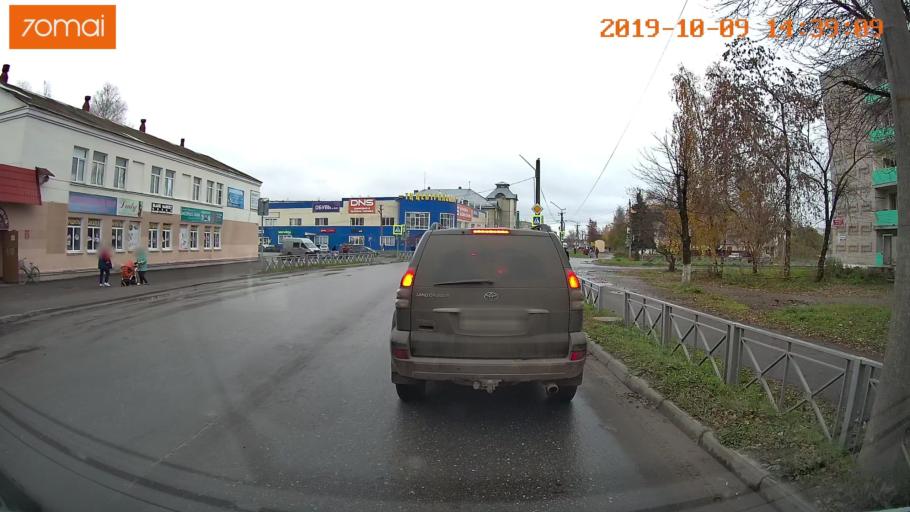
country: RU
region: Kostroma
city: Buy
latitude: 58.4771
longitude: 41.5386
